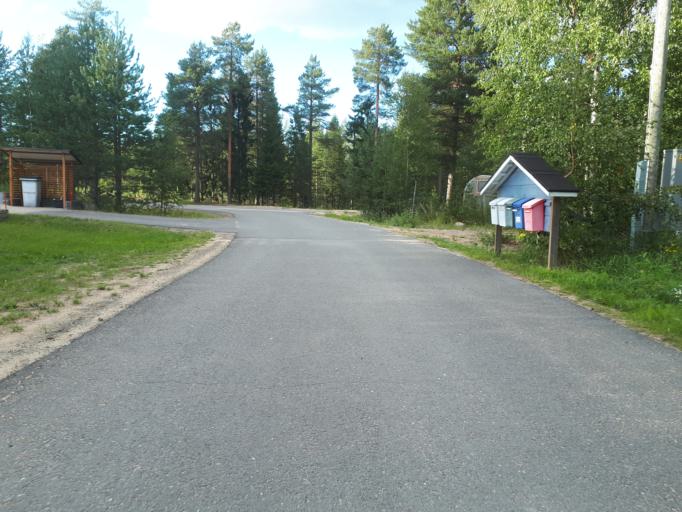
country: FI
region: Northern Ostrobothnia
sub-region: Oulunkaari
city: Ii
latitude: 65.3255
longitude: 25.4186
